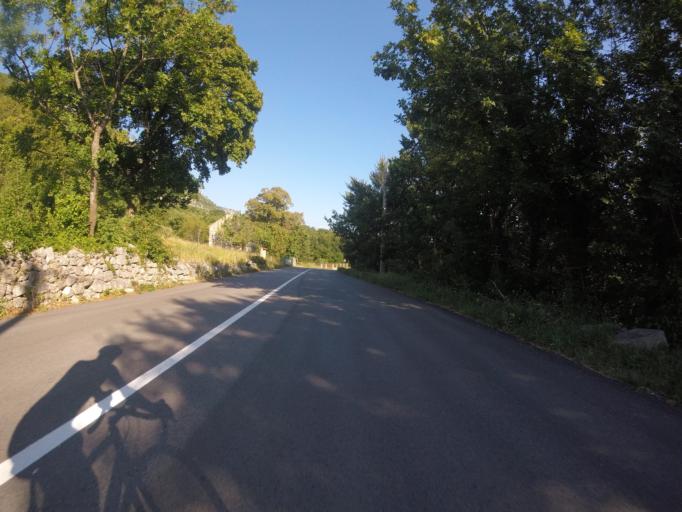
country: HR
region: Primorsko-Goranska
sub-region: Grad Crikvenica
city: Jadranovo
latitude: 45.2518
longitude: 14.6254
